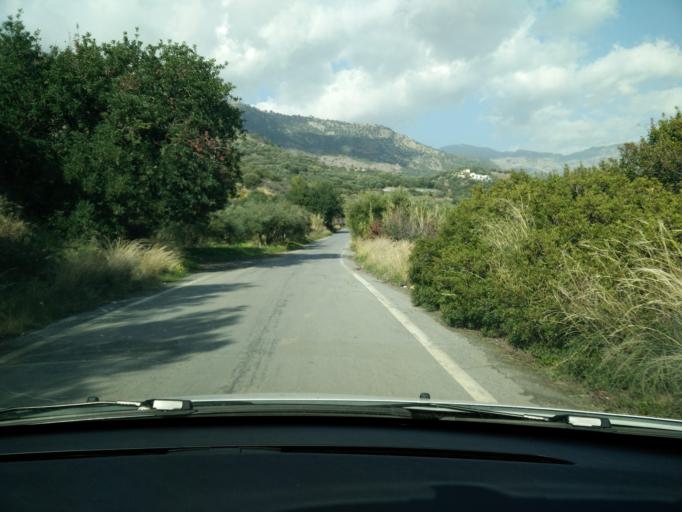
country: GR
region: Crete
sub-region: Nomos Lasithiou
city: Gra Liyia
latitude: 35.0237
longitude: 25.5815
